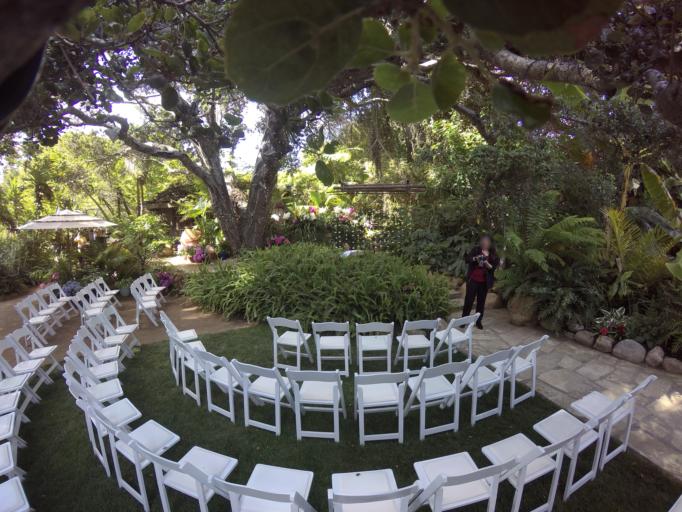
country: US
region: California
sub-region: Monterey County
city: Carmel Valley Village
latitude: 36.5248
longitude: -121.8158
